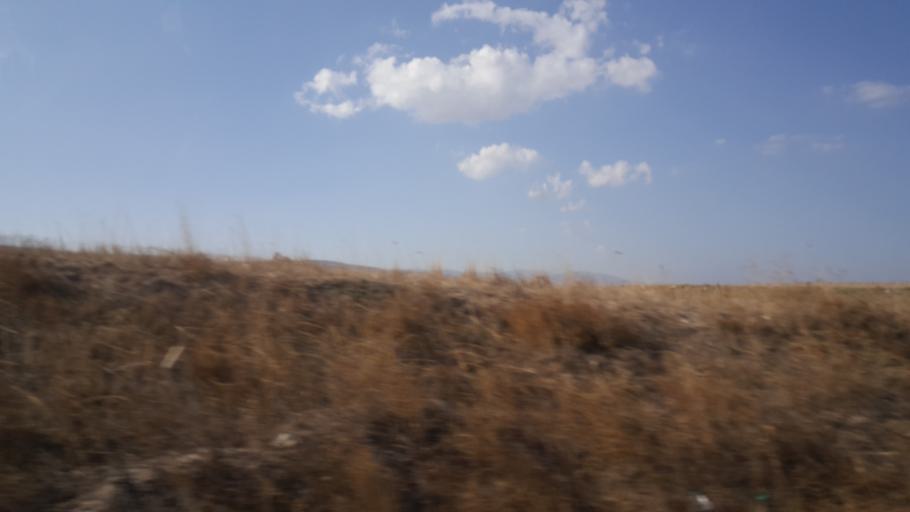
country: TR
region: Eskisehir
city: Kirka
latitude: 39.3089
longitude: 30.5357
